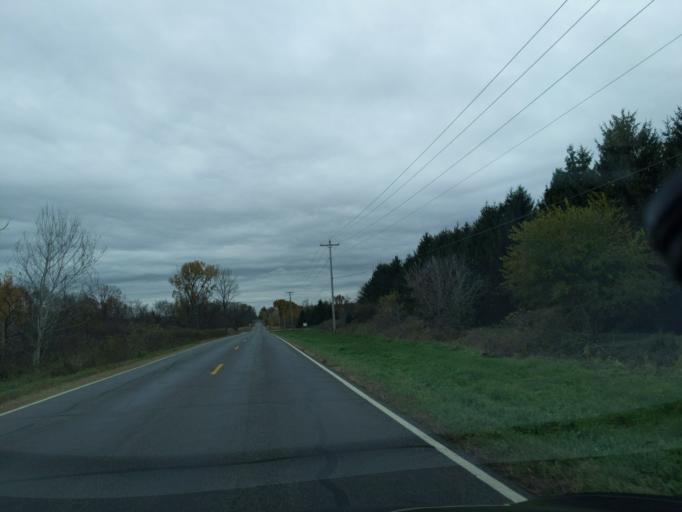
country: US
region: Michigan
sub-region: Jackson County
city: Spring Arbor
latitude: 42.2767
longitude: -84.6000
